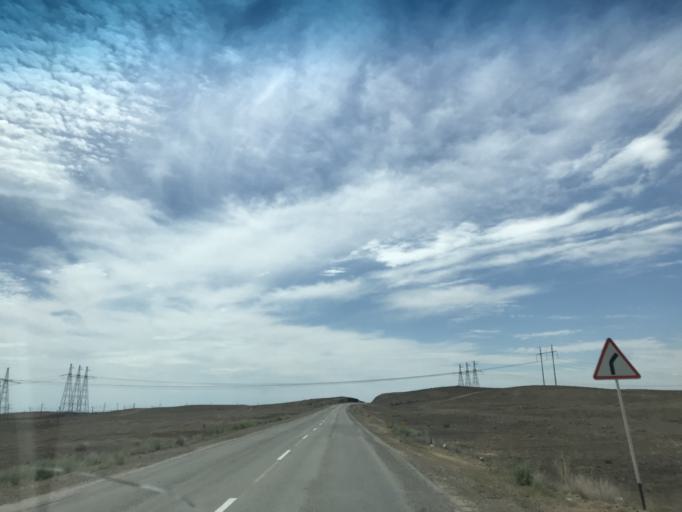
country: KZ
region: Almaty Oblysy
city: Ulken
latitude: 45.1402
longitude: 73.9619
